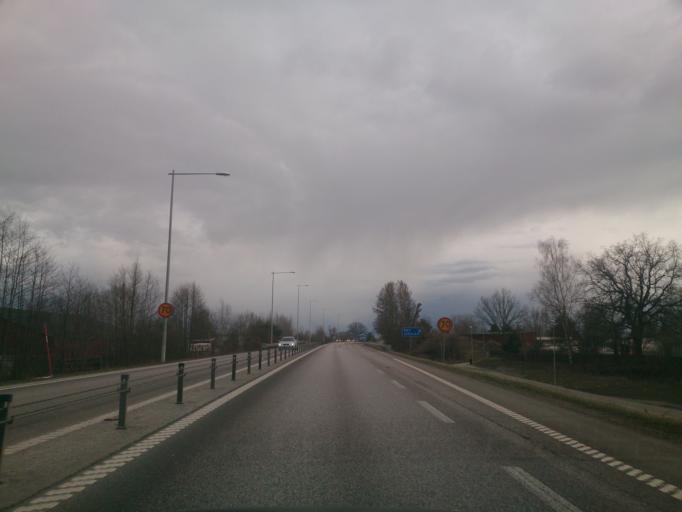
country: SE
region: OEstergoetland
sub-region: Norrkopings Kommun
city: Jursla
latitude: 58.6599
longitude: 16.1691
